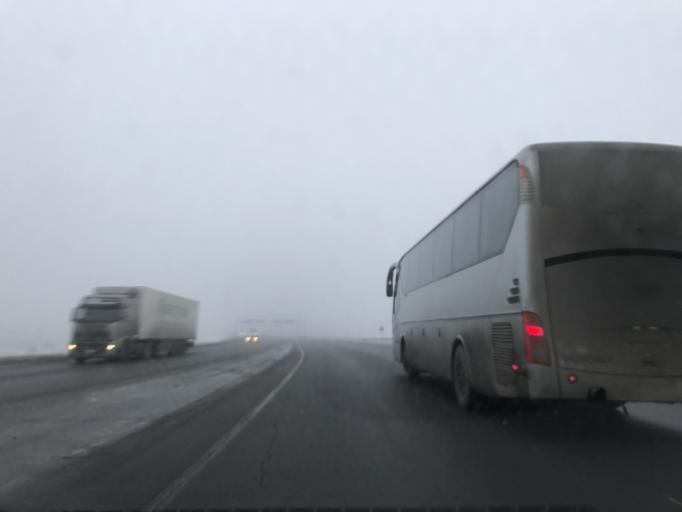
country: RU
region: Rostov
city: Grushevskaya
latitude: 47.4109
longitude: 39.9745
